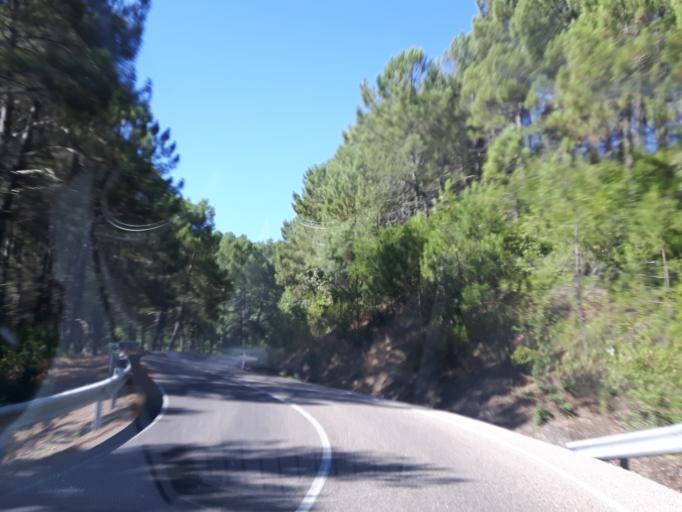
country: ES
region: Castille and Leon
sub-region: Provincia de Avila
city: Mombeltran
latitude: 40.2291
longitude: -5.0468
